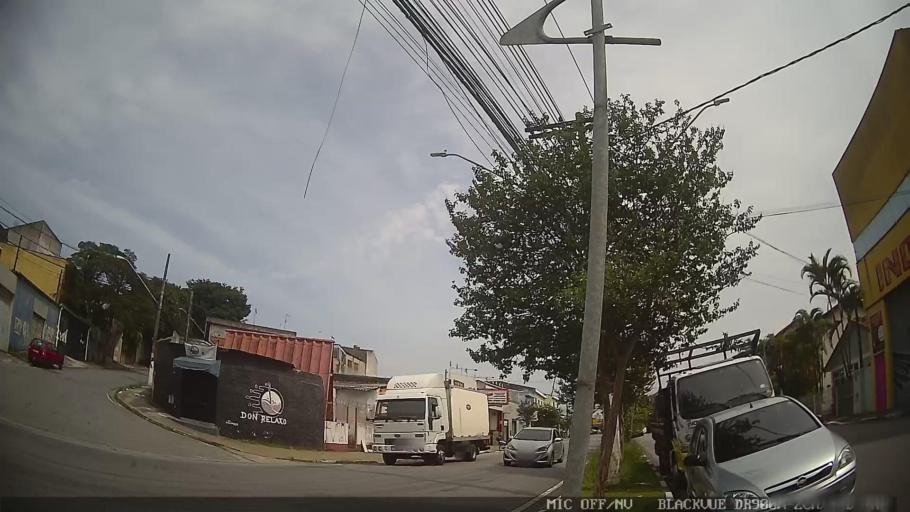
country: BR
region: Sao Paulo
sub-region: Poa
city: Poa
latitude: -23.5122
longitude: -46.3391
